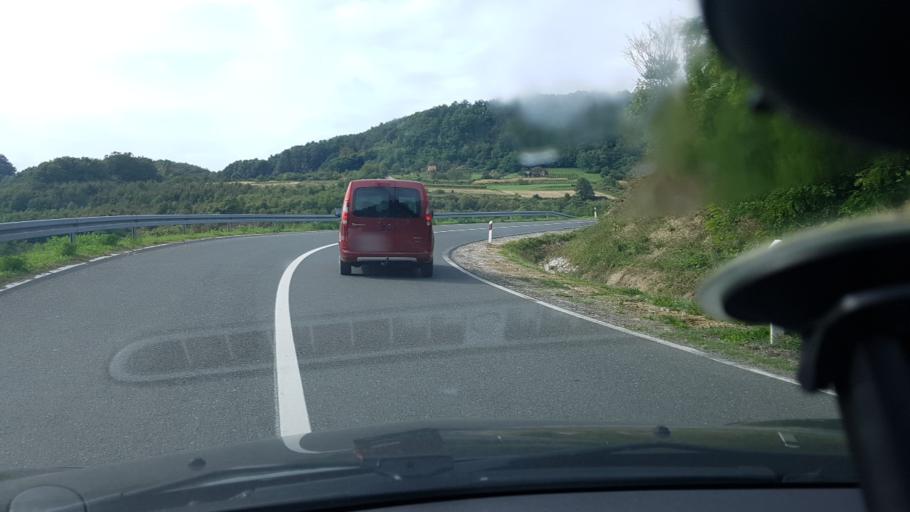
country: HR
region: Varazdinska
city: Ljubescica
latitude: 46.1094
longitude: 16.3558
